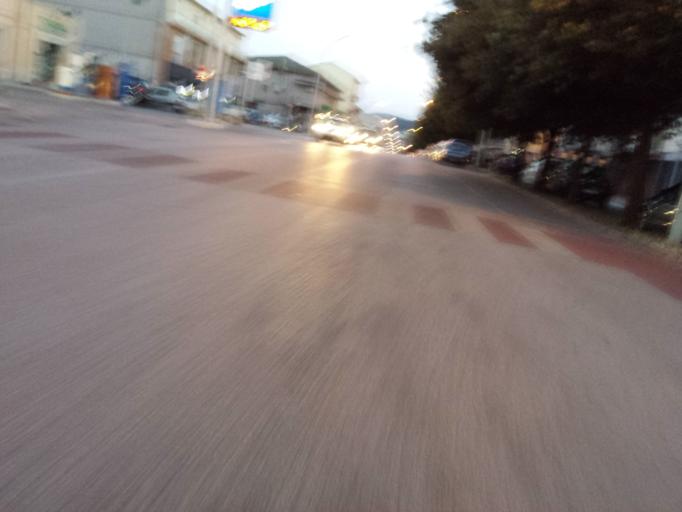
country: IT
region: Molise
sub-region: Provincia di Campobasso
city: Campobasso
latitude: 41.5671
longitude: 14.6727
